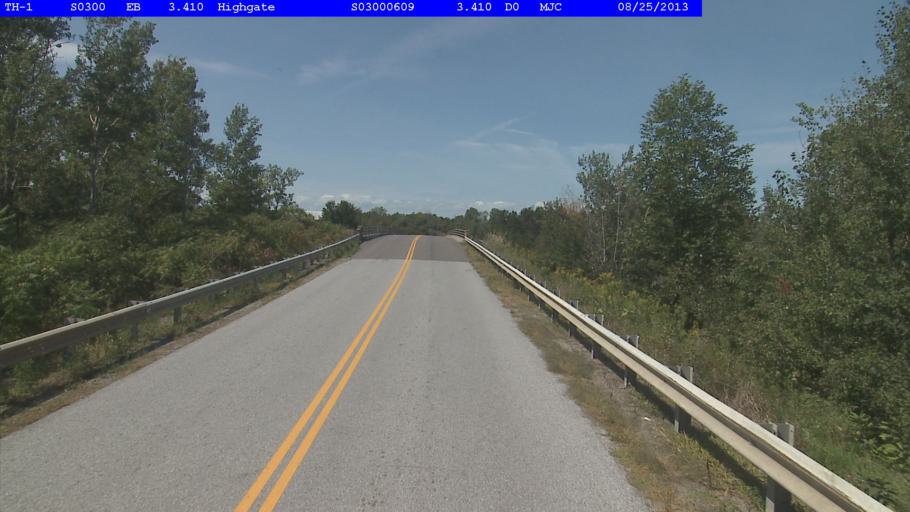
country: US
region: Vermont
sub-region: Franklin County
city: Swanton
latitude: 44.9694
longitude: -73.1042
